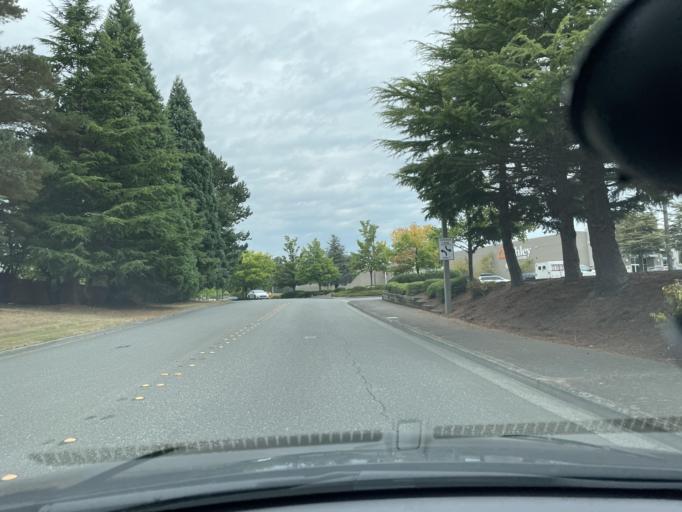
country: US
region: Washington
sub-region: Whatcom County
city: Bellingham
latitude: 48.7842
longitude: -122.4939
